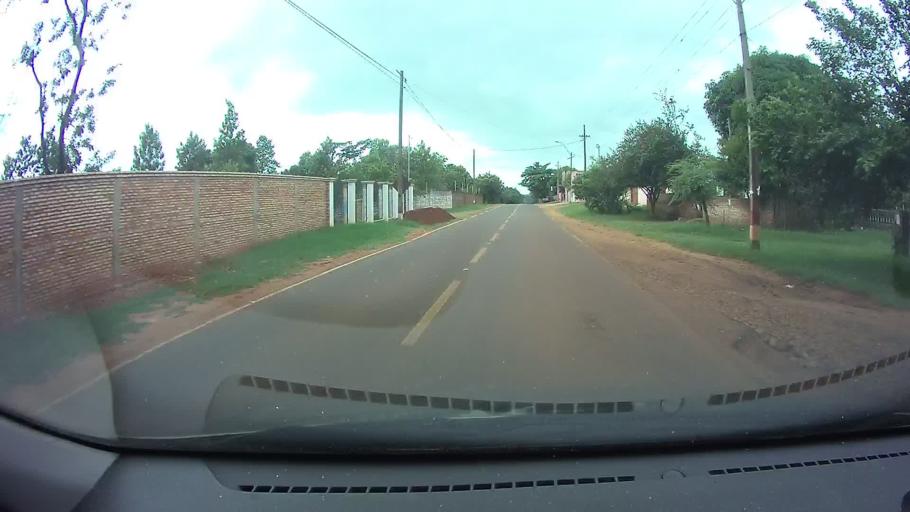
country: PY
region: Paraguari
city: Acahay
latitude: -25.9155
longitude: -57.1145
